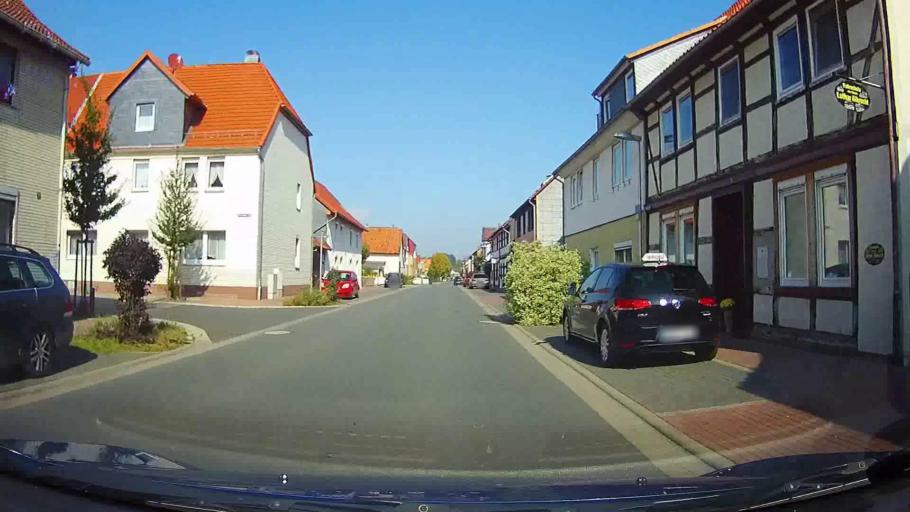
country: DE
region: Lower Saxony
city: Moringen
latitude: 51.6984
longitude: 9.8724
